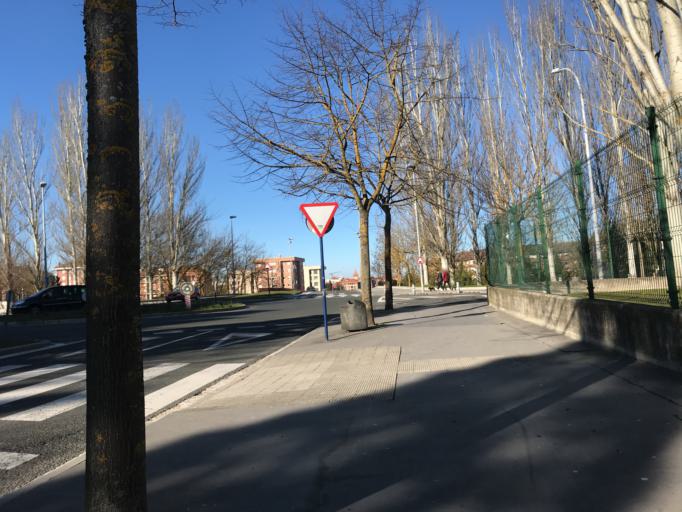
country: ES
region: Basque Country
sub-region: Provincia de Alava
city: Gasteiz / Vitoria
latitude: 42.8443
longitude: -2.6916
